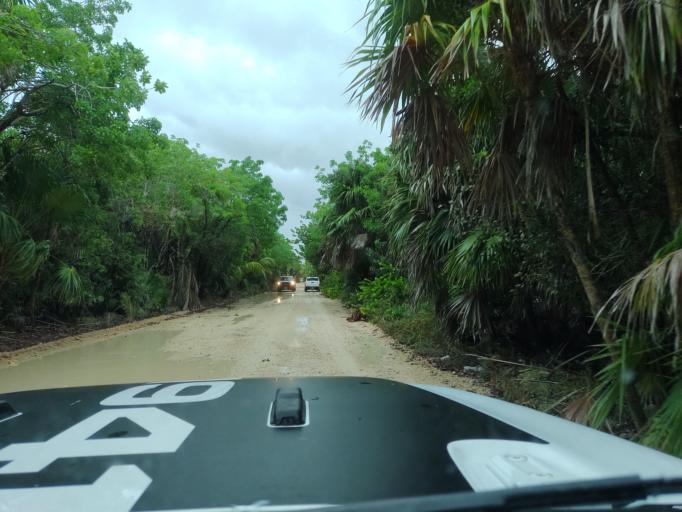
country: MX
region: Quintana Roo
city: Tulum
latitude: 20.0612
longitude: -87.4807
